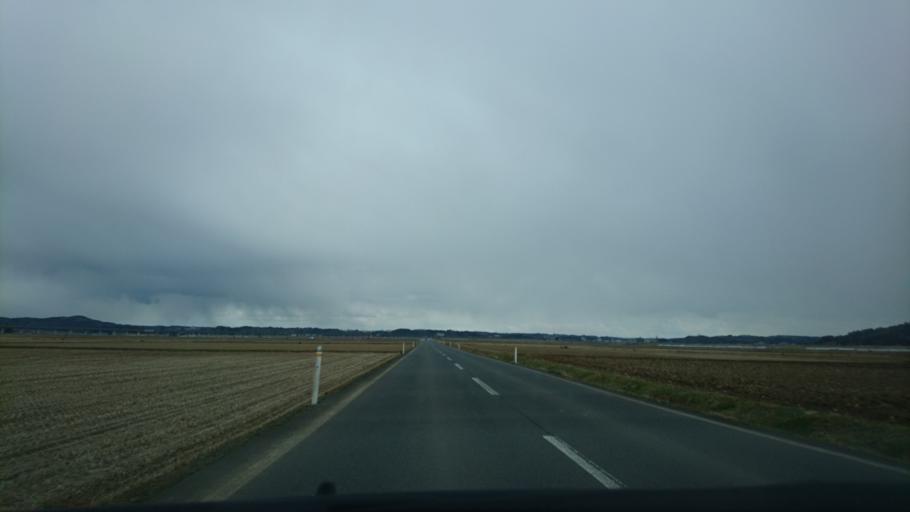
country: JP
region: Iwate
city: Ichinoseki
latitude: 38.9674
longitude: 141.1375
